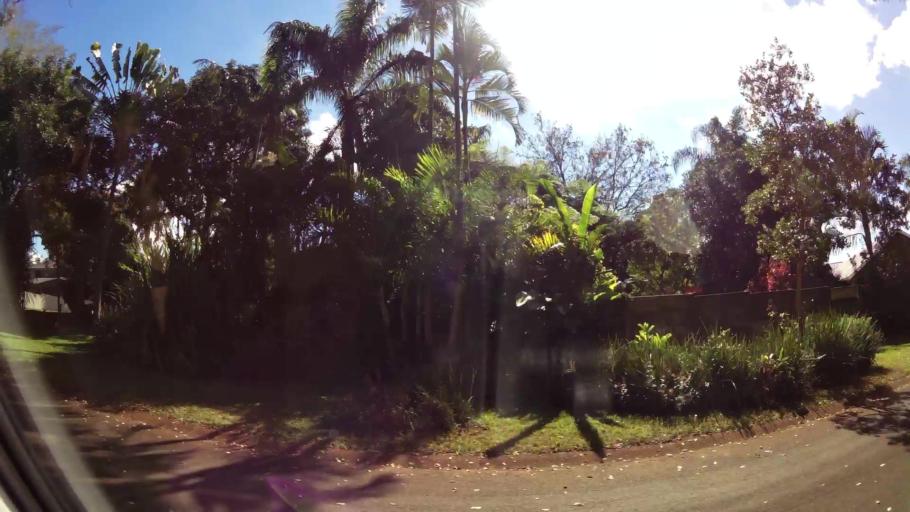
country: ZA
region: Limpopo
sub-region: Mopani District Municipality
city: Tzaneen
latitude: -23.8110
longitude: 30.1535
